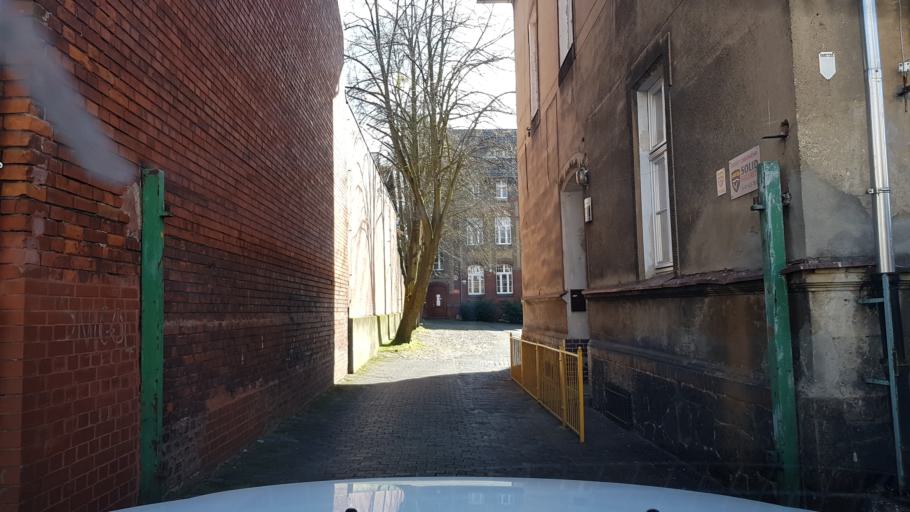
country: PL
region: West Pomeranian Voivodeship
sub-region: Szczecin
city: Szczecin
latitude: 53.4342
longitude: 14.5281
